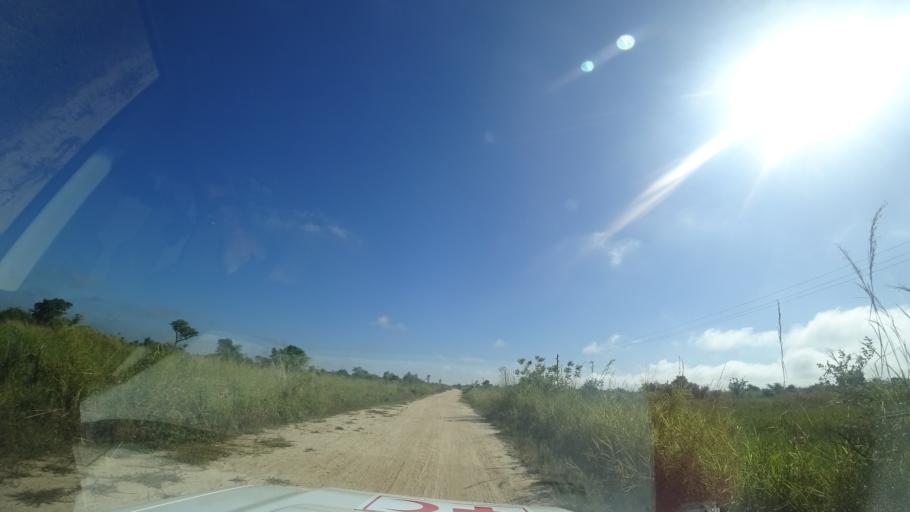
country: MZ
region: Sofala
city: Dondo
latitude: -19.4318
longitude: 34.5609
